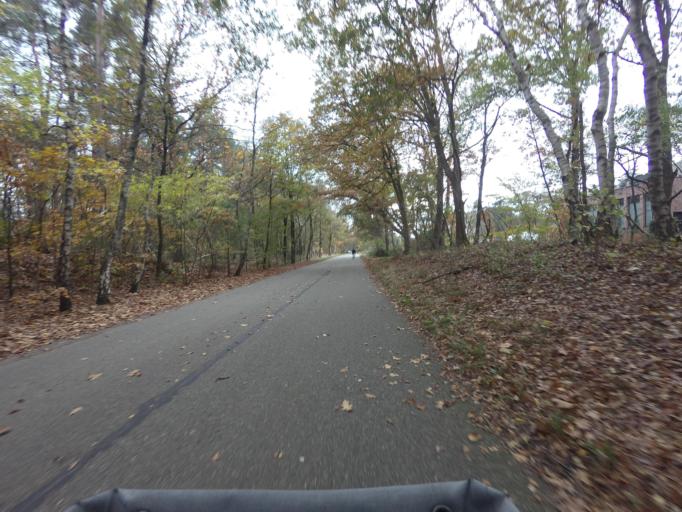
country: NL
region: North Holland
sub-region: Gemeente Laren
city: Laren
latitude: 52.2228
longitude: 5.2239
